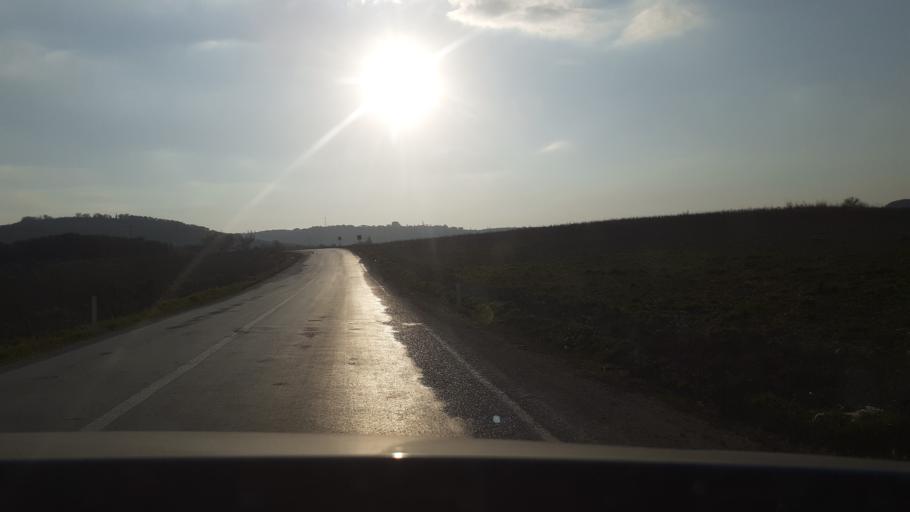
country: TR
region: Hatay
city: Oymakli
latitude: 36.1130
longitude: 36.2802
